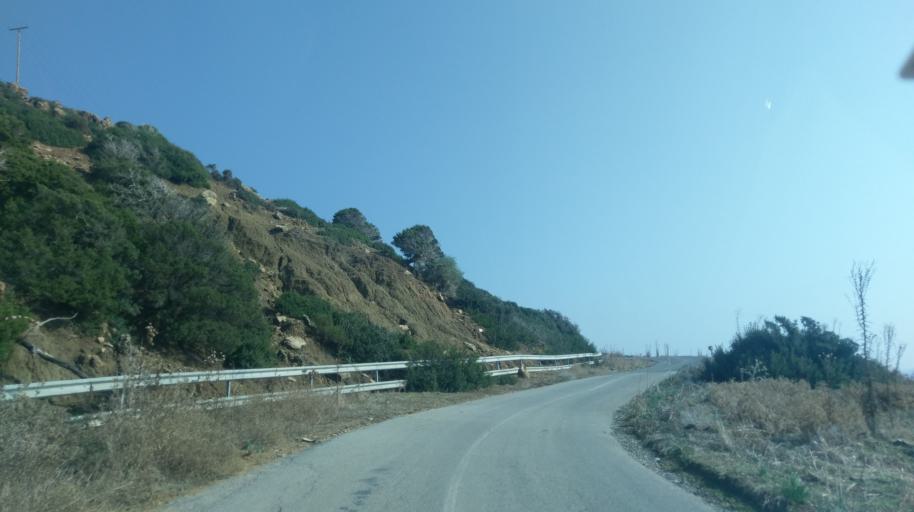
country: CY
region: Ammochostos
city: Rizokarpaso
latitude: 35.6447
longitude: 34.5555
